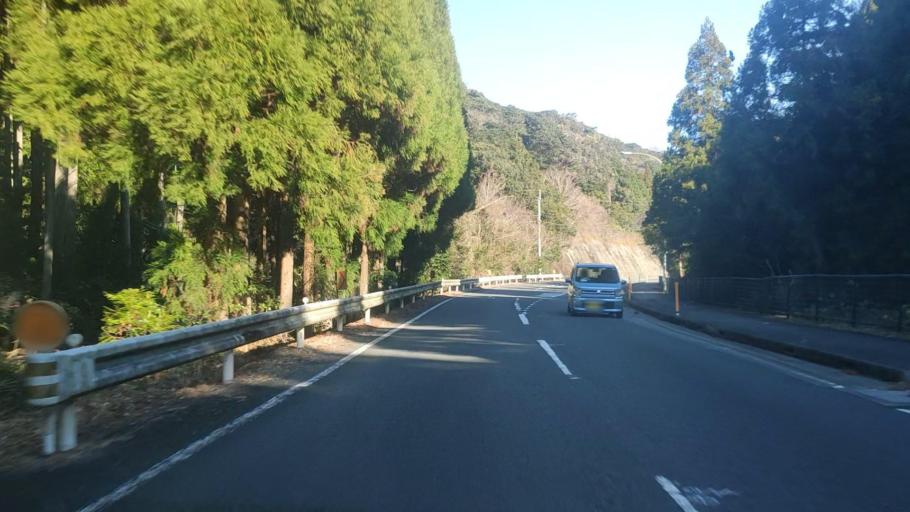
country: JP
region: Miyazaki
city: Nobeoka
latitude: 32.6954
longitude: 131.8122
